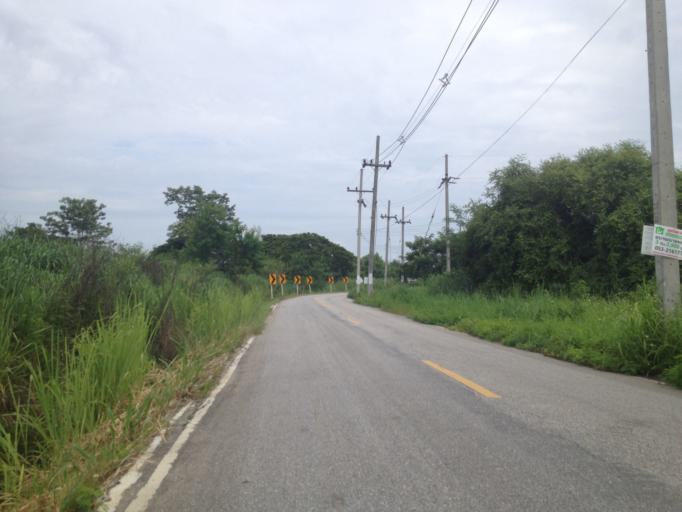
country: TH
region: Chiang Mai
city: Hang Dong
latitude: 18.7012
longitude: 98.9749
